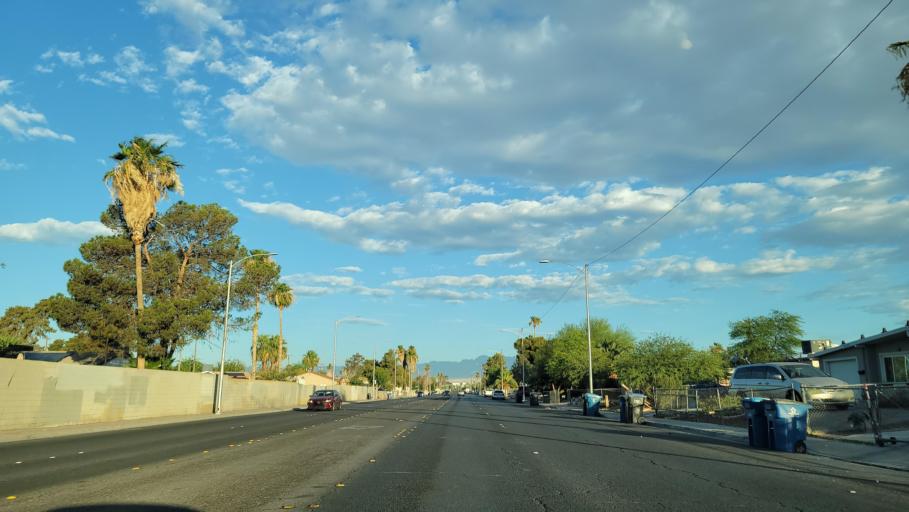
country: US
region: Nevada
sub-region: Clark County
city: North Las Vegas
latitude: 36.1882
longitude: -115.1009
